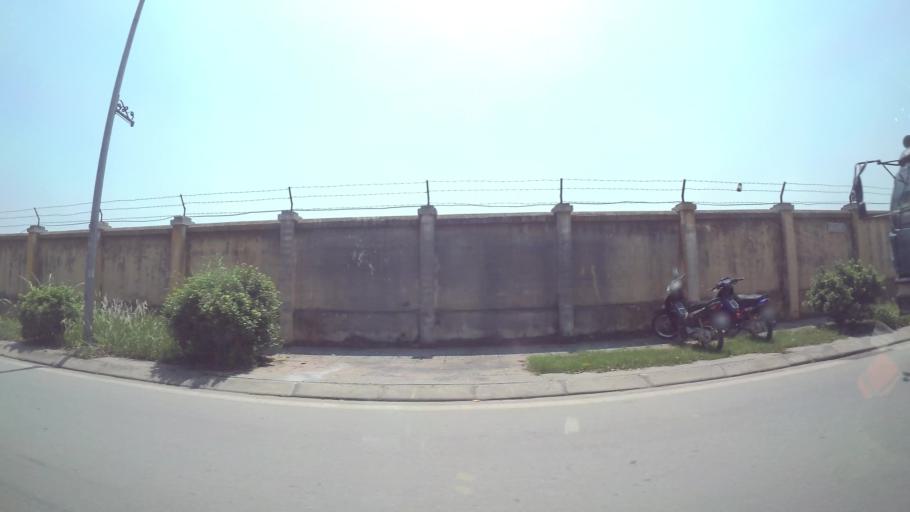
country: VN
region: Ha Noi
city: Hoan Kiem
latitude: 21.0479
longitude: 105.8886
